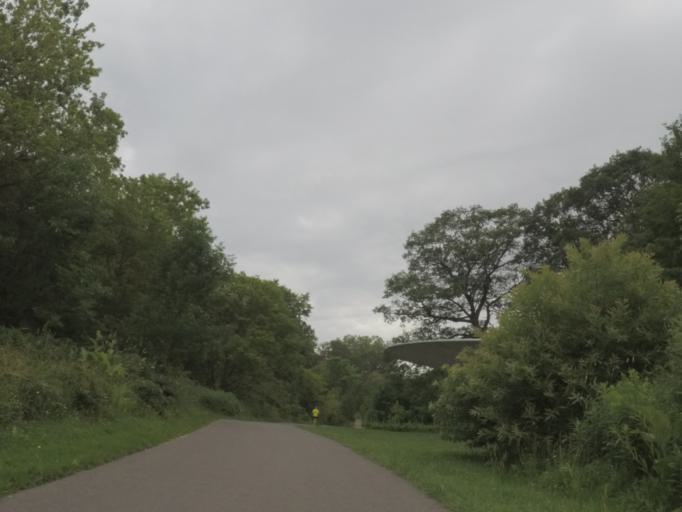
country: CA
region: Ontario
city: Etobicoke
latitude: 43.6364
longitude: -79.4798
